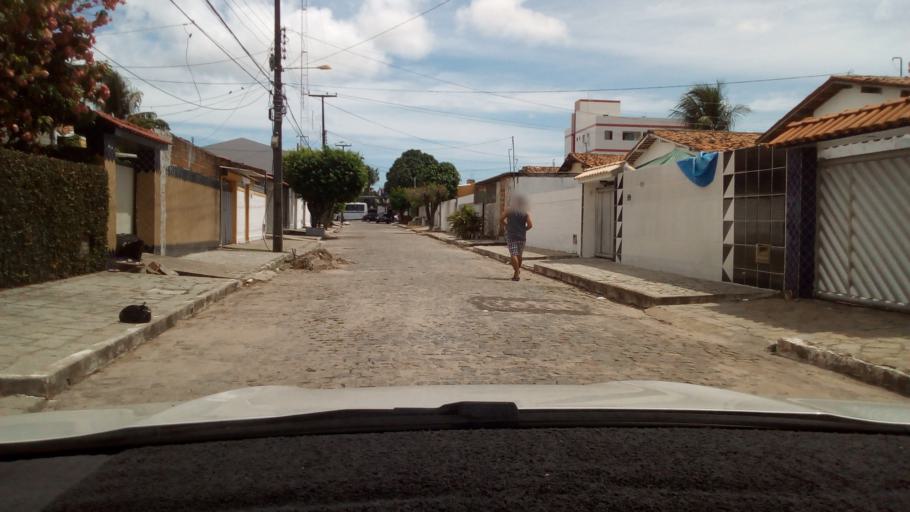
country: BR
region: Paraiba
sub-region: Joao Pessoa
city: Joao Pessoa
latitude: -7.1692
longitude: -34.8309
